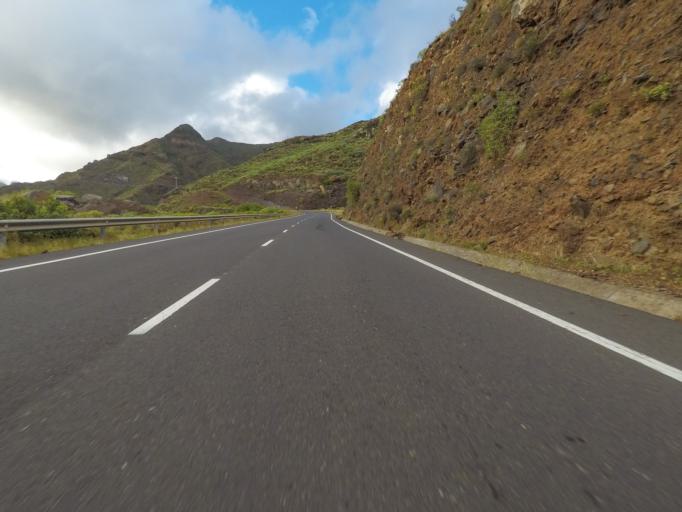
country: ES
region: Canary Islands
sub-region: Provincia de Santa Cruz de Tenerife
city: San Sebastian de la Gomera
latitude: 28.1187
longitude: -17.1425
